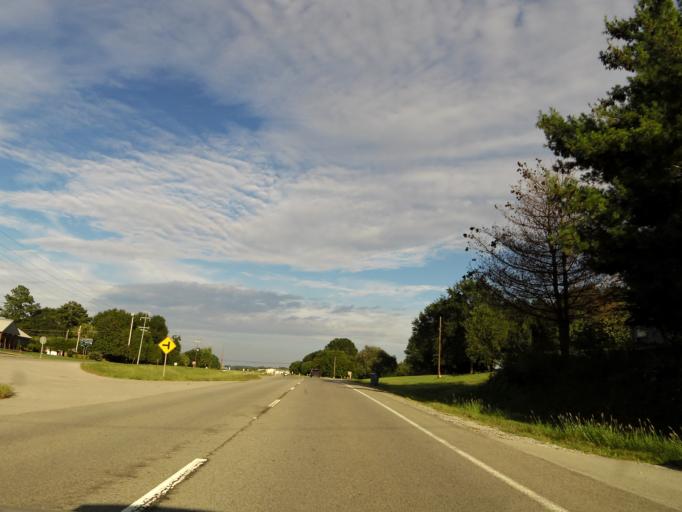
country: US
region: Alabama
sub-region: Lauderdale County
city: Killen
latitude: 34.8600
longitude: -87.4440
